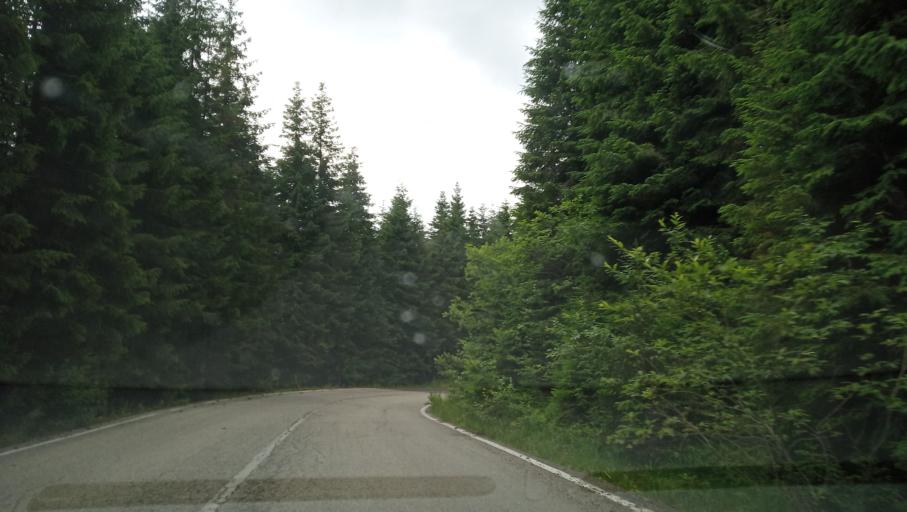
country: RO
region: Valcea
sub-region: Comuna Voineasa
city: Voineasa
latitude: 45.4225
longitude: 23.7611
